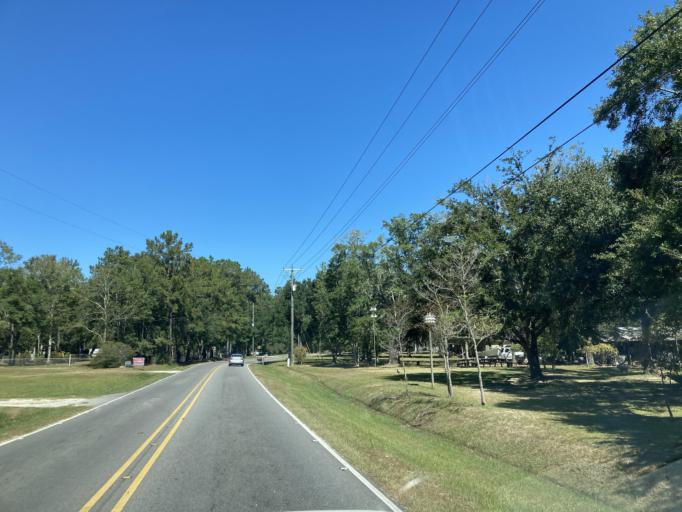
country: US
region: Mississippi
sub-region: Jackson County
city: Saint Martin
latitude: 30.4723
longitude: -88.8822
